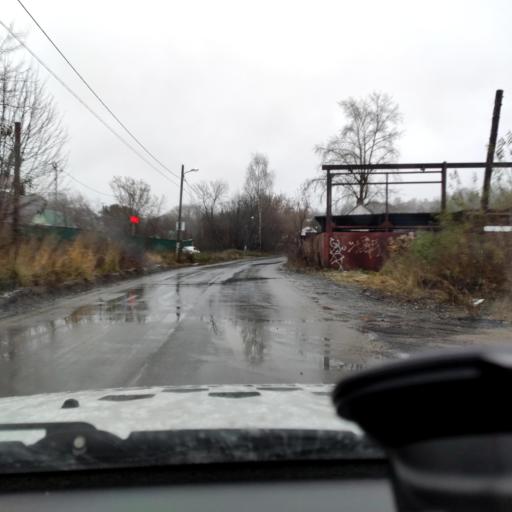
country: RU
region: Perm
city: Perm
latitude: 58.0585
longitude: 56.3299
